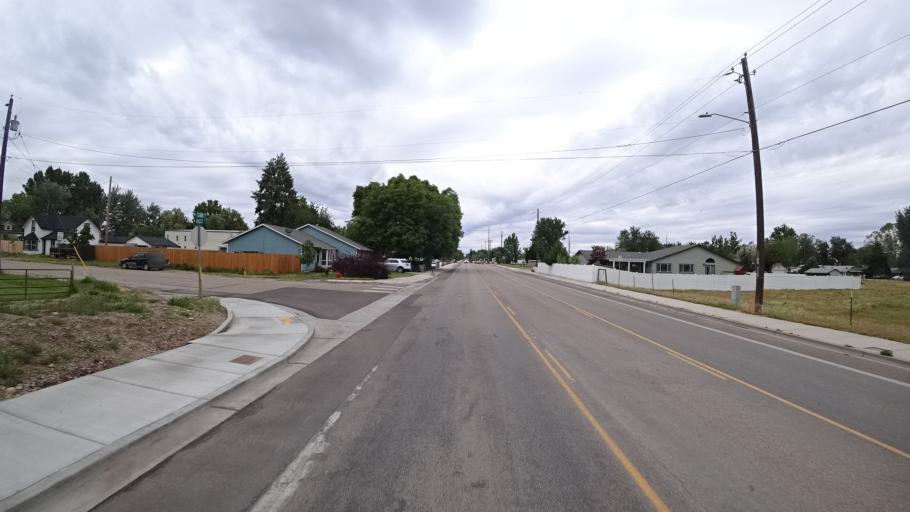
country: US
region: Idaho
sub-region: Ada County
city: Star
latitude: 43.6945
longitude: -116.4933
